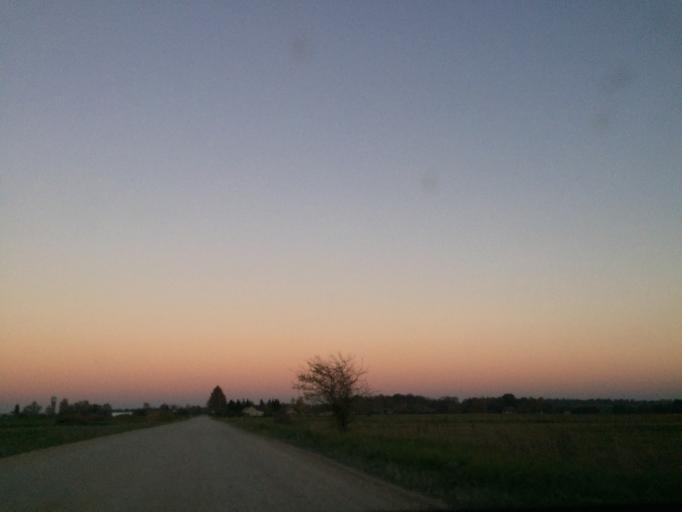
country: LT
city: Akmene
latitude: 56.3766
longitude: 22.7312
